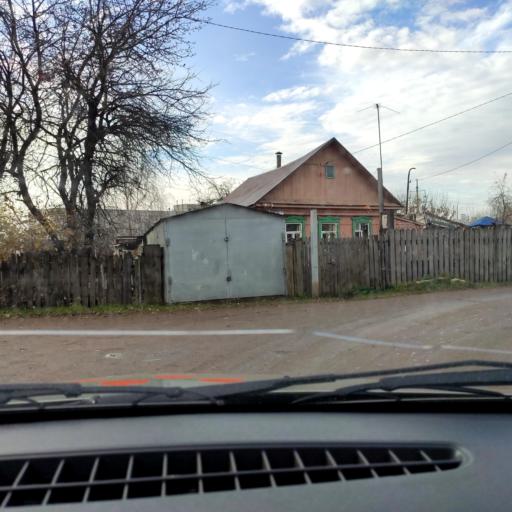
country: RU
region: Bashkortostan
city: Ufa
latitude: 54.7917
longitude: 56.0926
